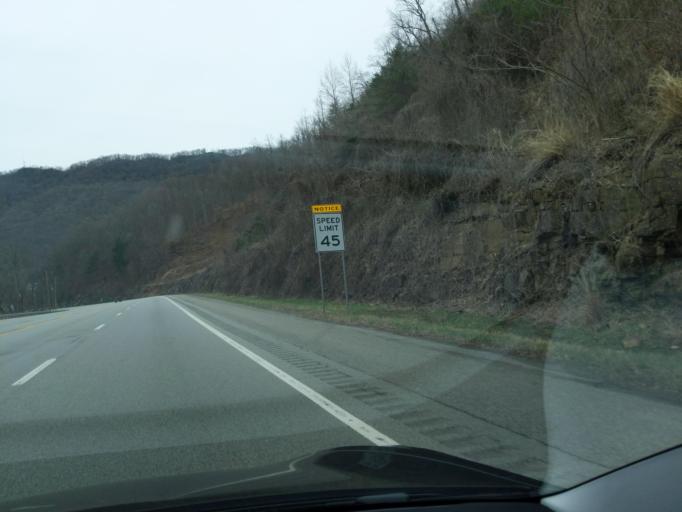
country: US
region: Kentucky
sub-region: Bell County
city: Pineville
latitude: 36.7662
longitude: -83.7148
